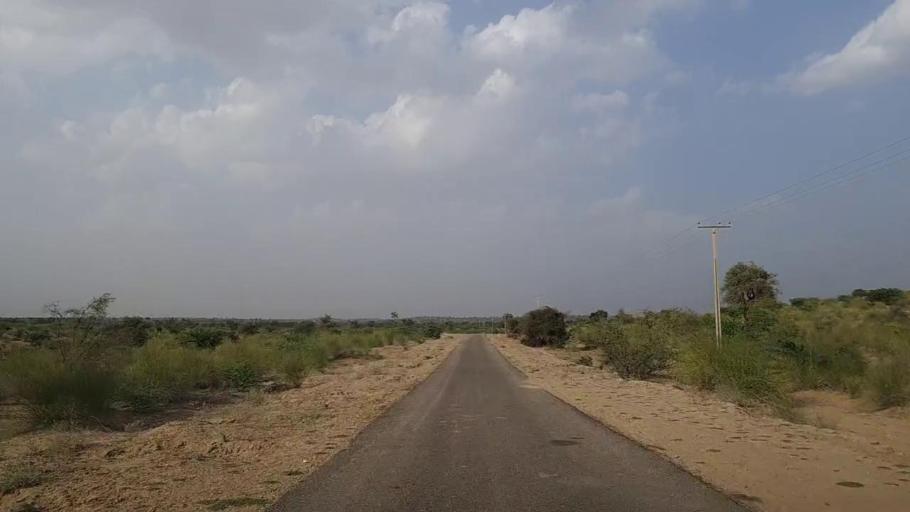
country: PK
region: Sindh
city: Islamkot
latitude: 24.7916
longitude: 70.2015
